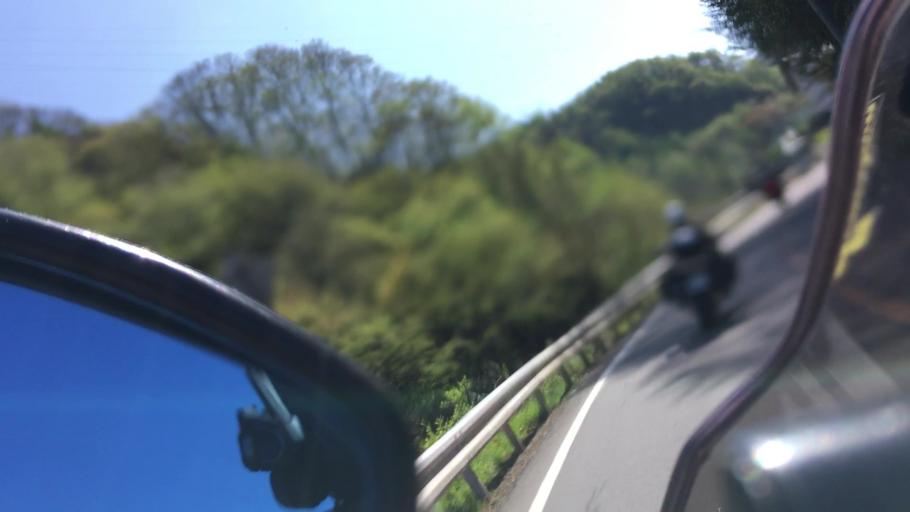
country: JP
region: Nagano
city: Komoro
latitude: 36.4869
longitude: 138.4862
